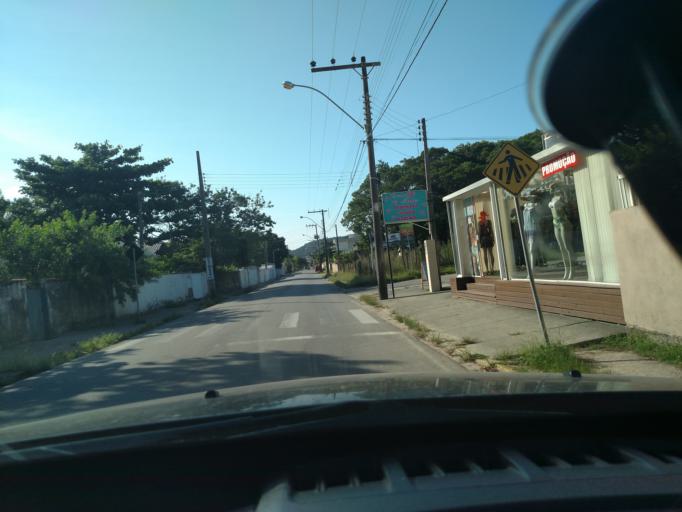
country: BR
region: Santa Catarina
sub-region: Porto Belo
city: Porto Belo
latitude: -27.1951
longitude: -48.5014
